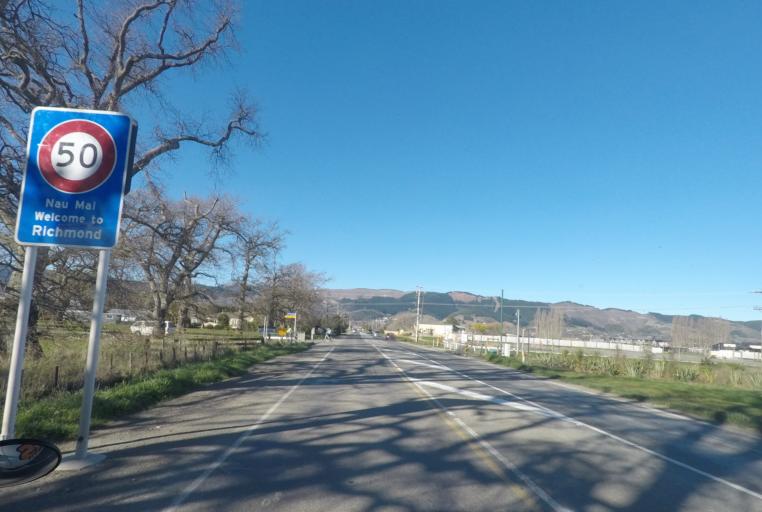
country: NZ
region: Tasman
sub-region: Tasman District
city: Richmond
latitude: -41.3274
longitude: 173.1716
